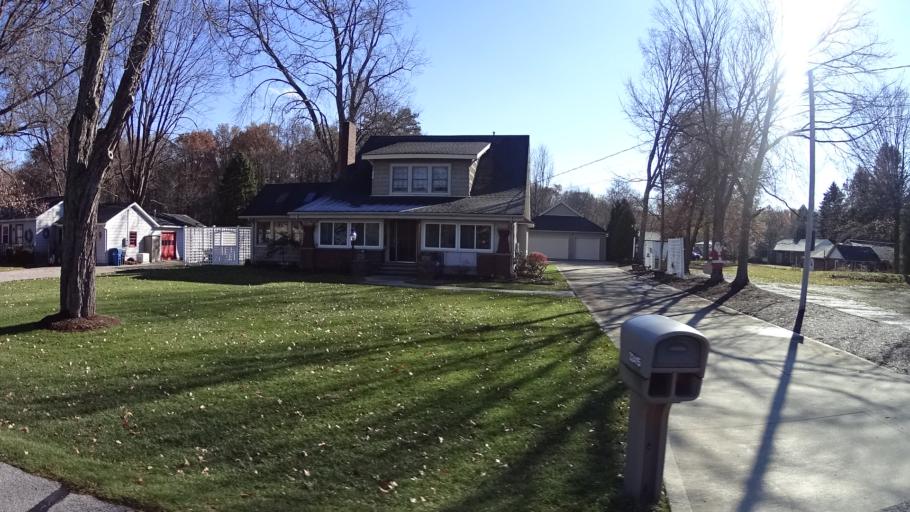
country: US
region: Ohio
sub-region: Lorain County
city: North Ridgeville
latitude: 41.4101
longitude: -81.9761
